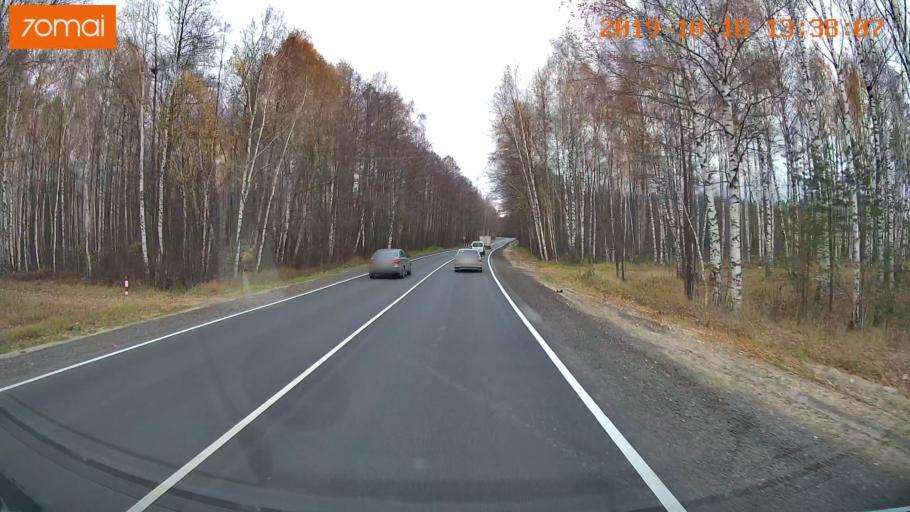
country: RU
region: Rjazan
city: Solotcha
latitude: 54.8864
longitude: 40.0012
